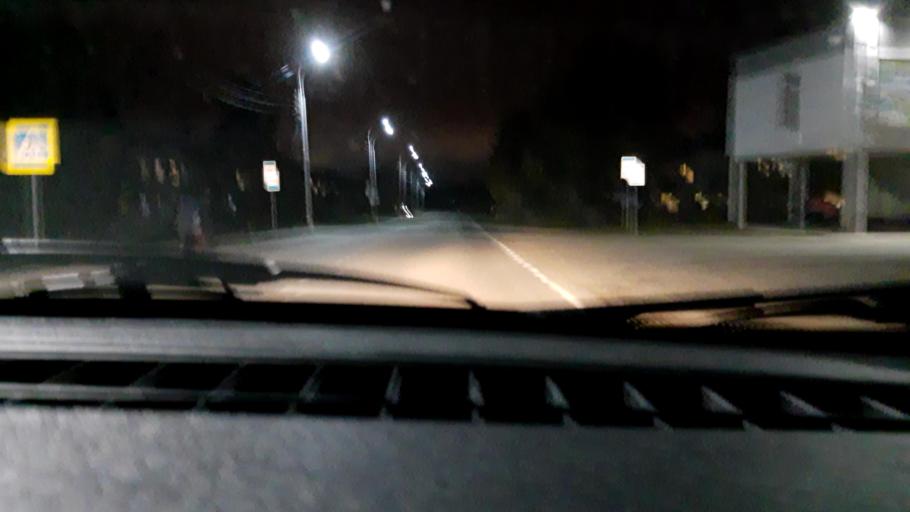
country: RU
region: Bashkortostan
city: Mikhaylovka
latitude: 54.8113
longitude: 55.8082
